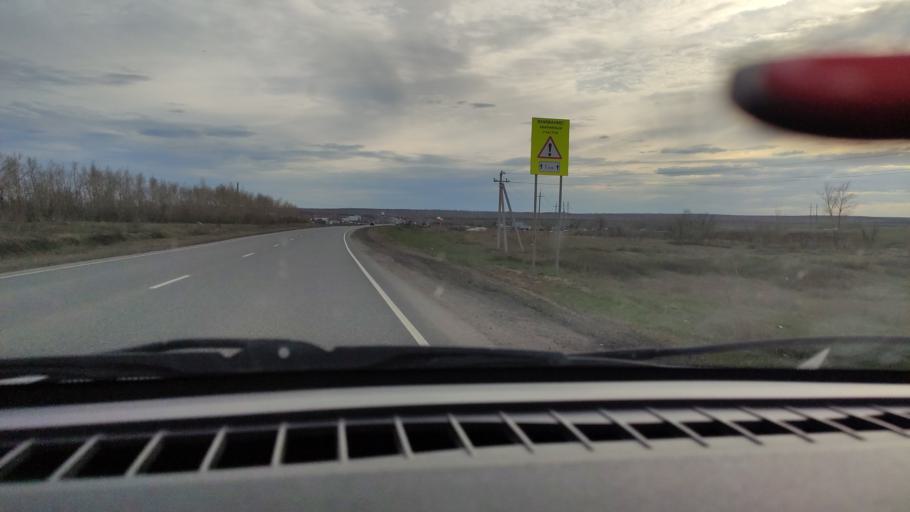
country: RU
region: Orenburg
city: Tatarskaya Kargala
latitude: 52.0306
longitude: 55.2386
